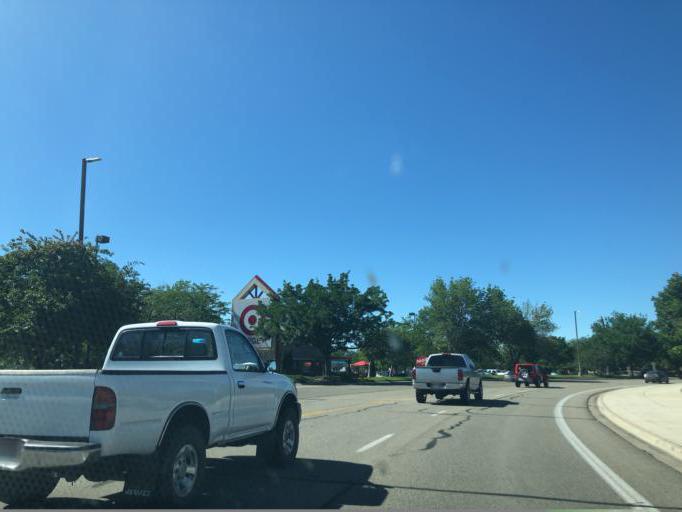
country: US
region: Idaho
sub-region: Ada County
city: Garden City
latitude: 43.6090
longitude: -116.2846
